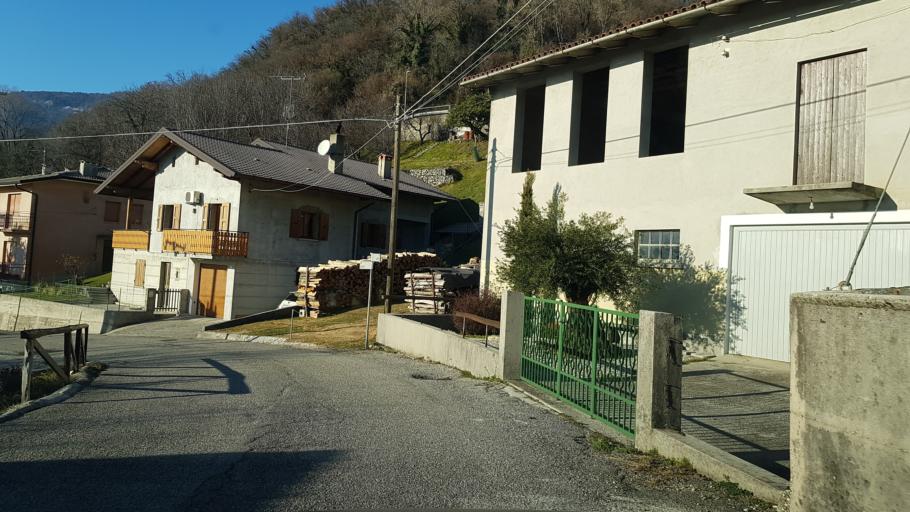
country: IT
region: Friuli Venezia Giulia
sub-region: Provincia di Udine
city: Forgaria nel Friuli
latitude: 46.2253
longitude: 12.9749
